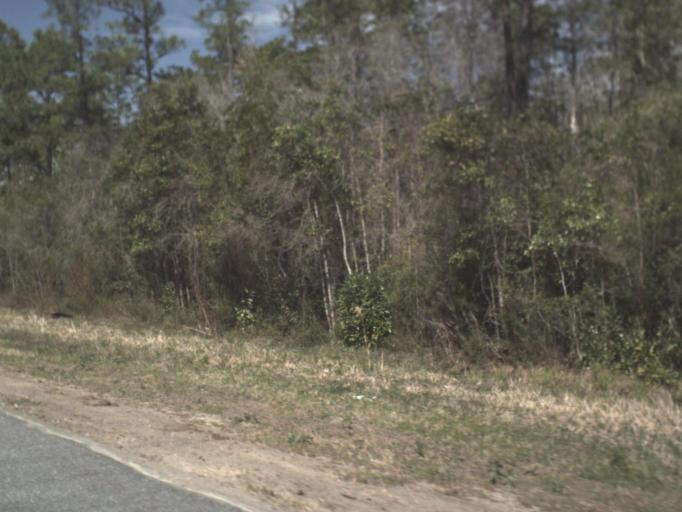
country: US
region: Florida
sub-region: Wakulla County
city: Crawfordville
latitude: 30.3140
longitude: -84.4401
